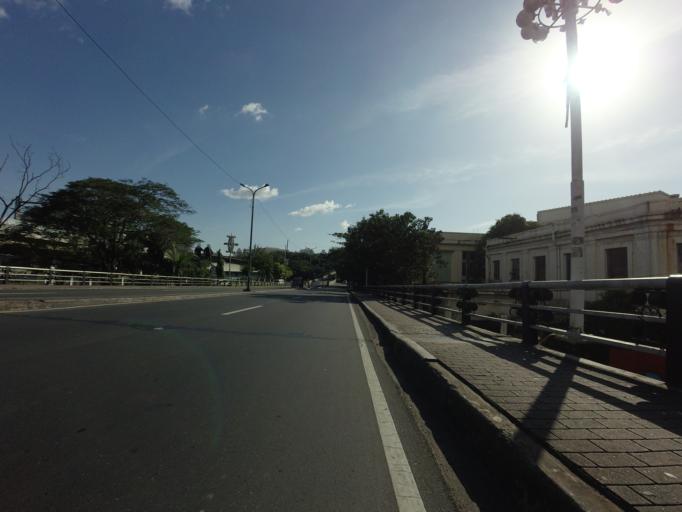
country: PH
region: Metro Manila
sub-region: City of Manila
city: Quiapo
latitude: 14.5964
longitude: 120.9803
